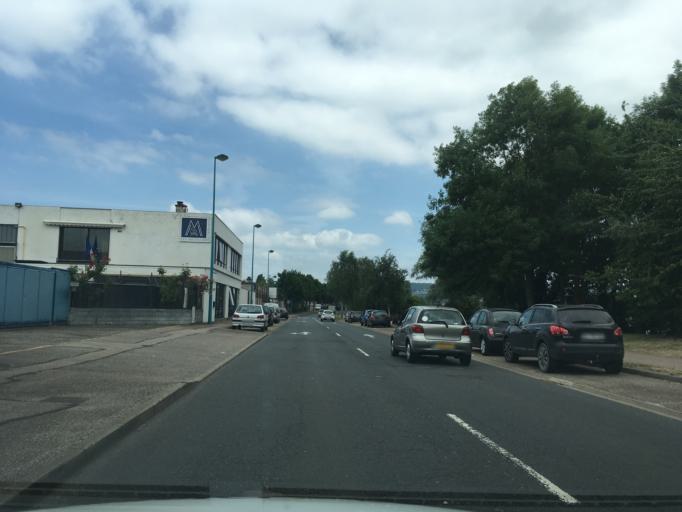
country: FR
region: Lorraine
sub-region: Departement de Meurthe-et-Moselle
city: Tomblaine
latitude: 48.6830
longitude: 6.2065
